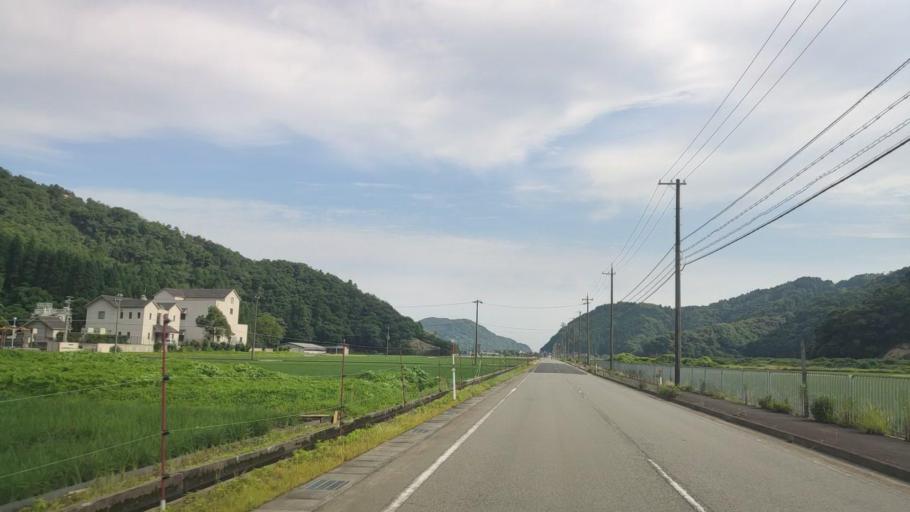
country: JP
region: Hyogo
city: Toyooka
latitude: 35.6252
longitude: 134.8411
